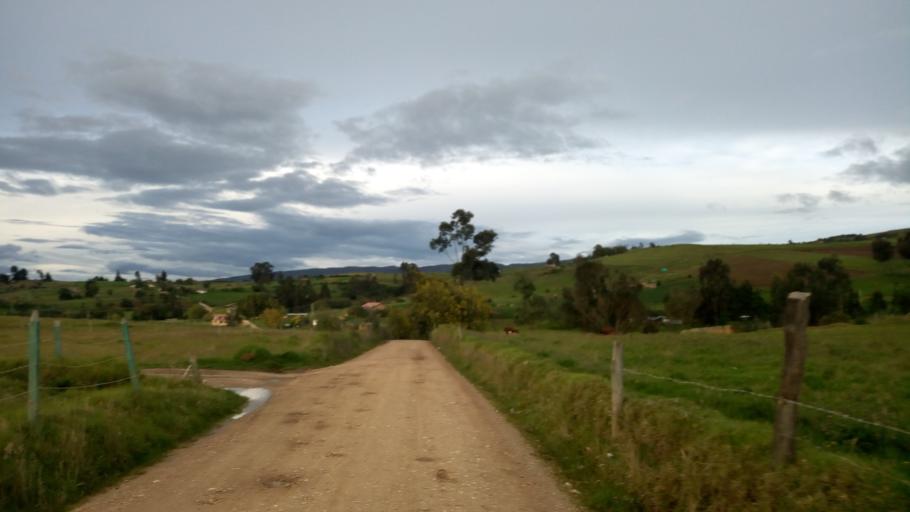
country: CO
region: Boyaca
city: Toca
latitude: 5.5774
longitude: -73.1799
